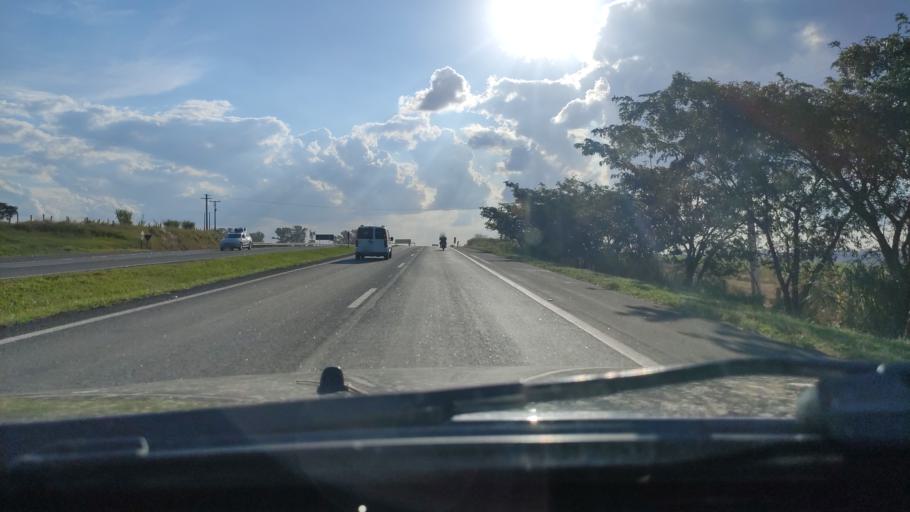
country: BR
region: Sao Paulo
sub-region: Mogi-Mirim
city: Mogi Mirim
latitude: -22.4559
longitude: -46.9140
